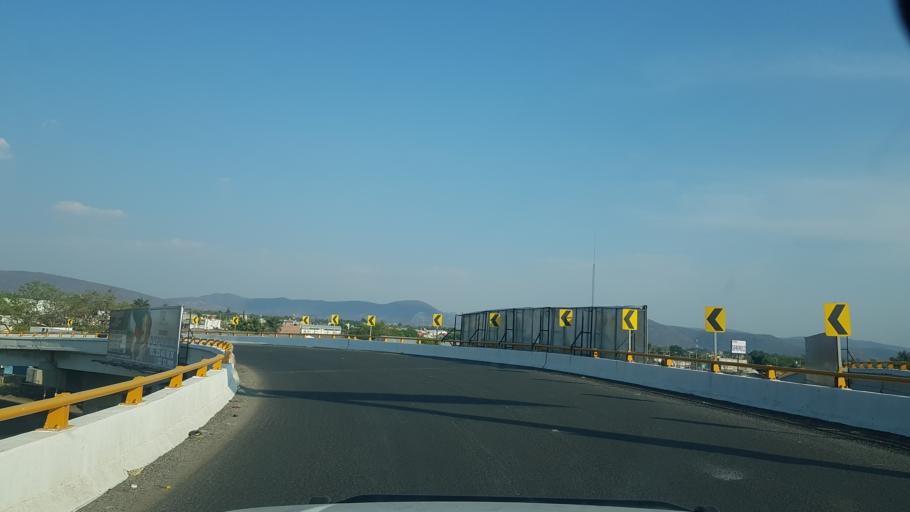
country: MX
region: Puebla
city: Izucar de Matamoros
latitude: 18.6002
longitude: -98.4807
